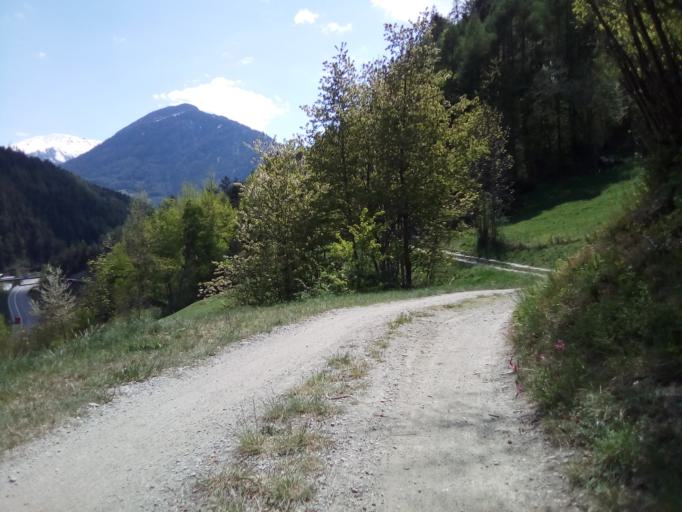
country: CH
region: Valais
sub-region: Entremont District
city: Orsieres
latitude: 46.0498
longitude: 7.1469
